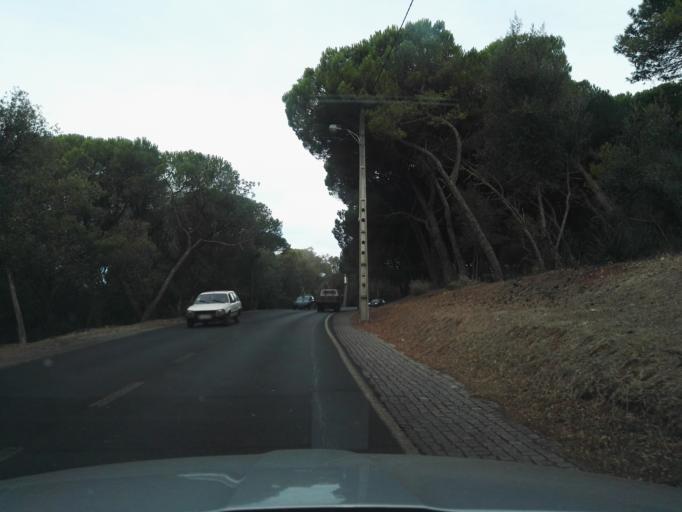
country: PT
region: Lisbon
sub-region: Odivelas
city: Pontinha
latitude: 38.7279
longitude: -9.1968
